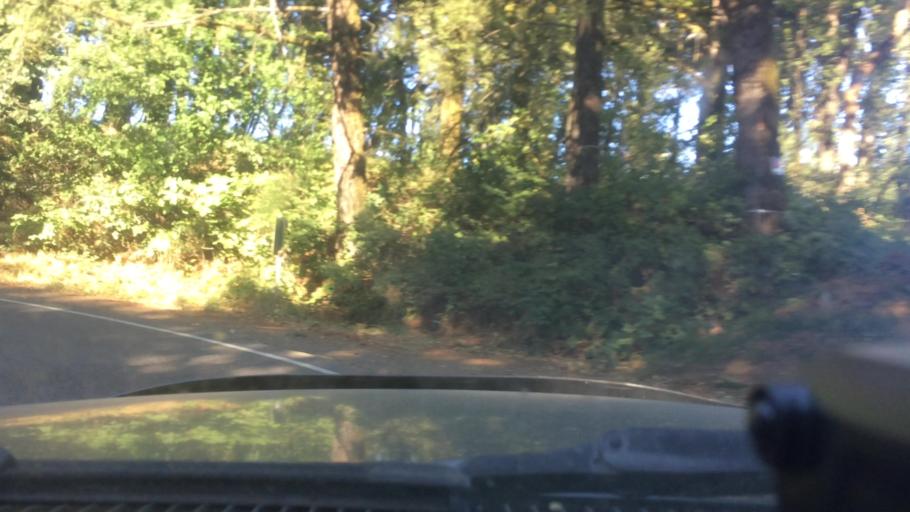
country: US
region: Oregon
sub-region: Yamhill County
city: Newberg
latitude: 45.3298
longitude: -122.9291
